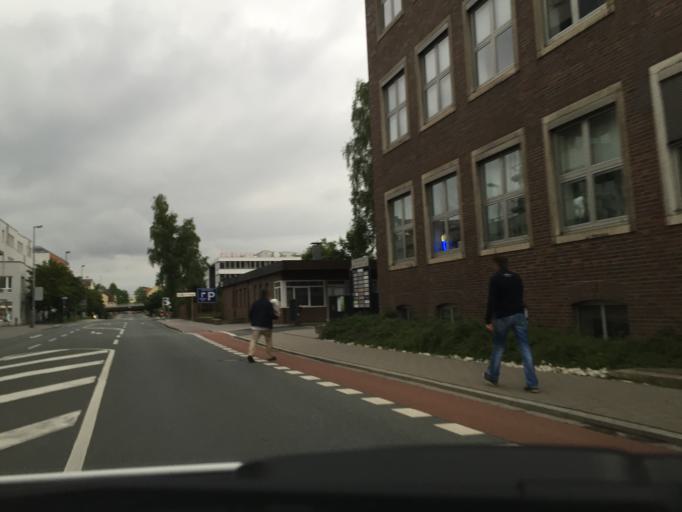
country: DE
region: Bavaria
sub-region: Regierungsbezirk Mittelfranken
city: Erlangen
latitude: 49.5909
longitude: 11.0047
